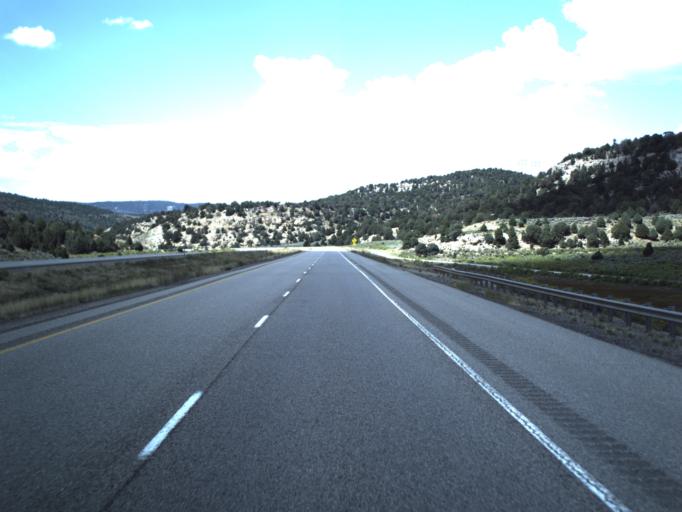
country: US
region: Utah
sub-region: Sevier County
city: Salina
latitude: 38.7981
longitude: -111.5119
